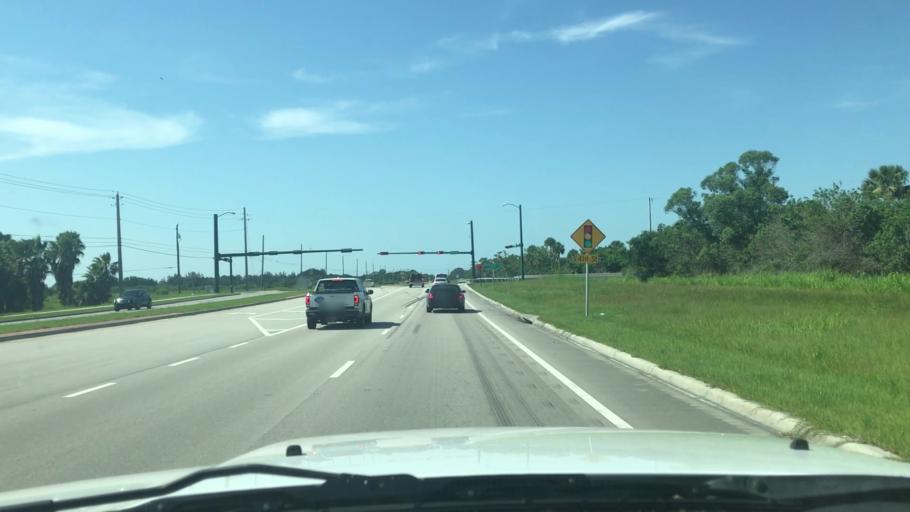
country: US
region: Florida
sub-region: Indian River County
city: West Vero Corridor
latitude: 27.6668
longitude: -80.4630
